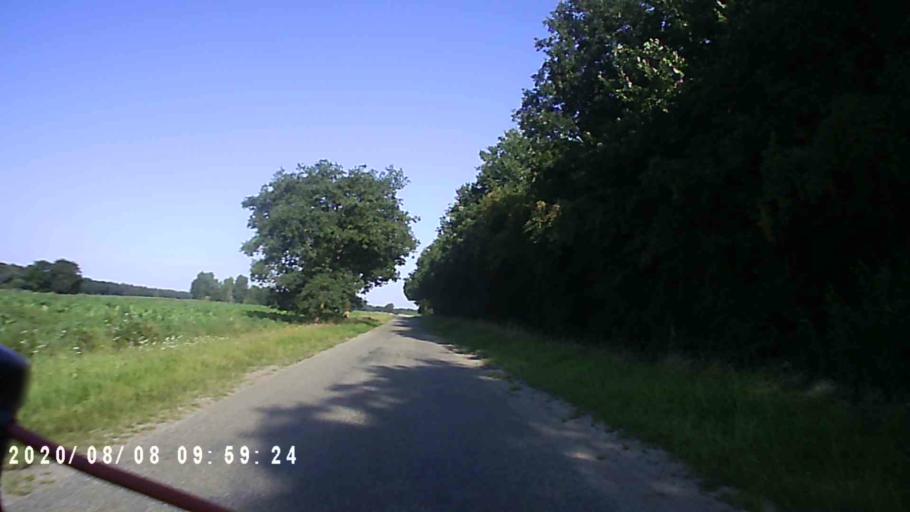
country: NL
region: Groningen
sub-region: Gemeente Leek
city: Leek
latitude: 53.1005
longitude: 6.4035
